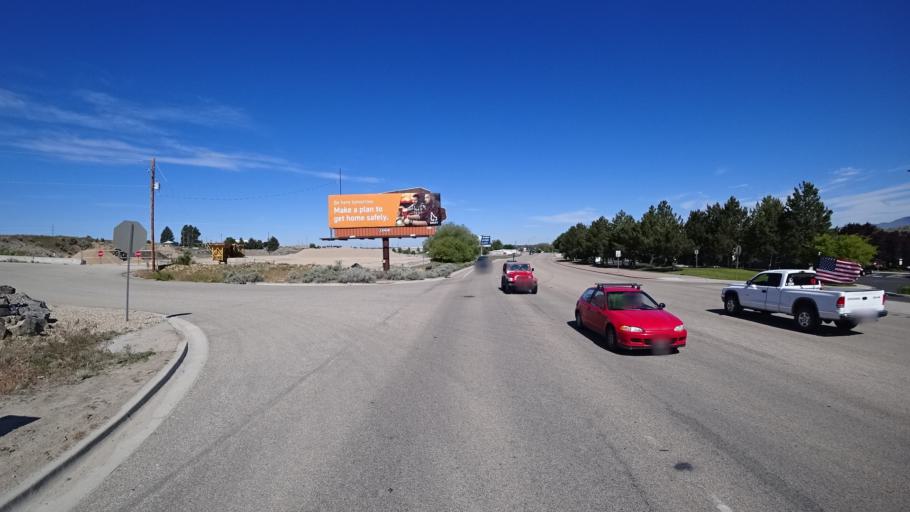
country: US
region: Idaho
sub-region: Ada County
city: Boise
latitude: 43.5653
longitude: -116.1782
